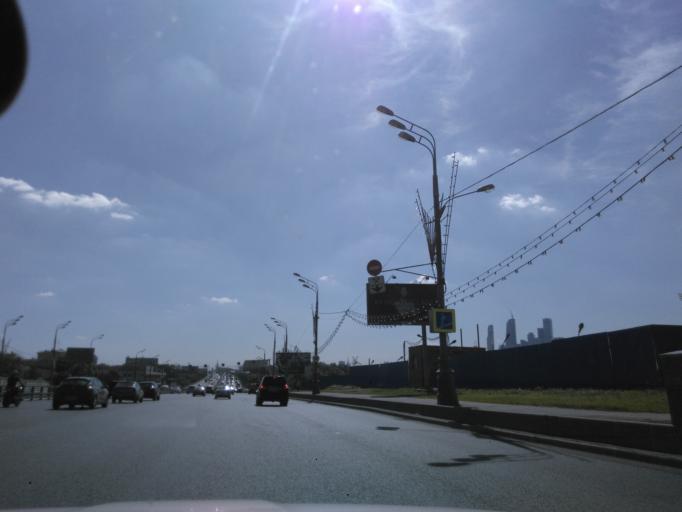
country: RU
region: Moskovskaya
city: Khoroshevo-Mnevniki
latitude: 55.7717
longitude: 37.4966
